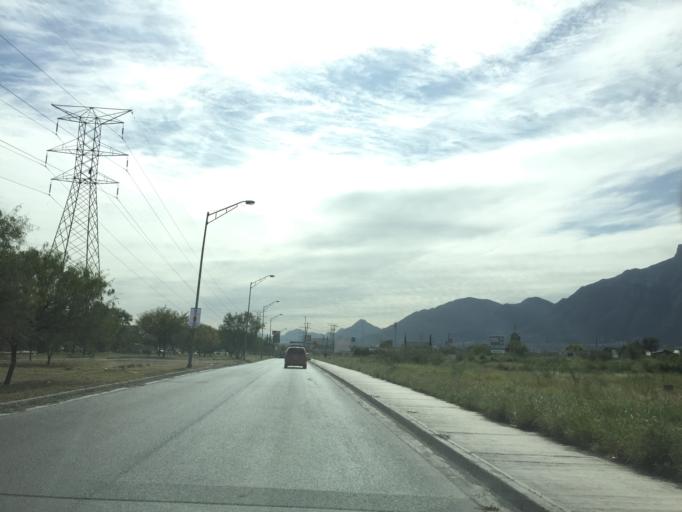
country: MX
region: Nuevo Leon
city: Guadalupe
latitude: 25.6985
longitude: -100.2136
